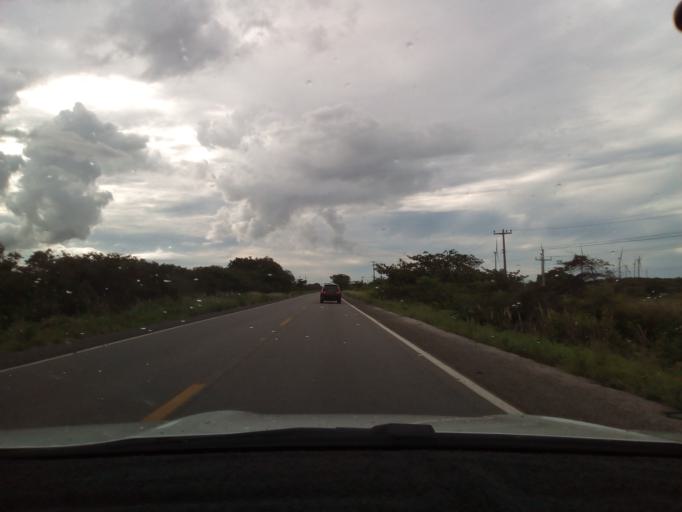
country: BR
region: Ceara
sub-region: Aracati
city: Aracati
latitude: -4.6322
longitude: -37.6393
